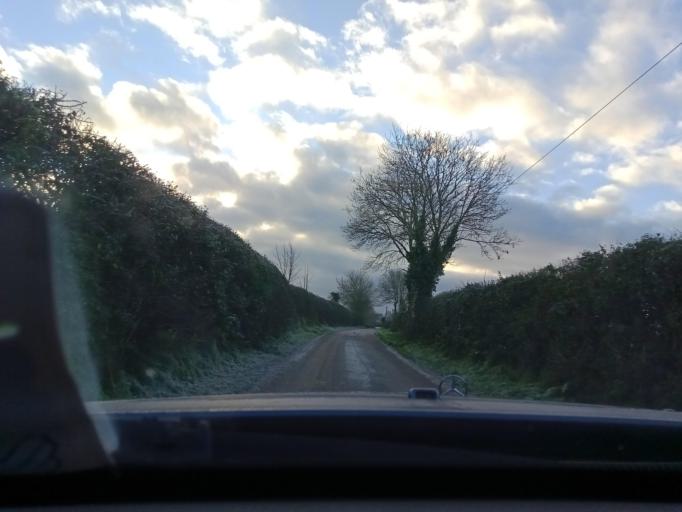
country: IE
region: Leinster
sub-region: County Carlow
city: Bagenalstown
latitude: 52.6421
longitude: -7.0174
